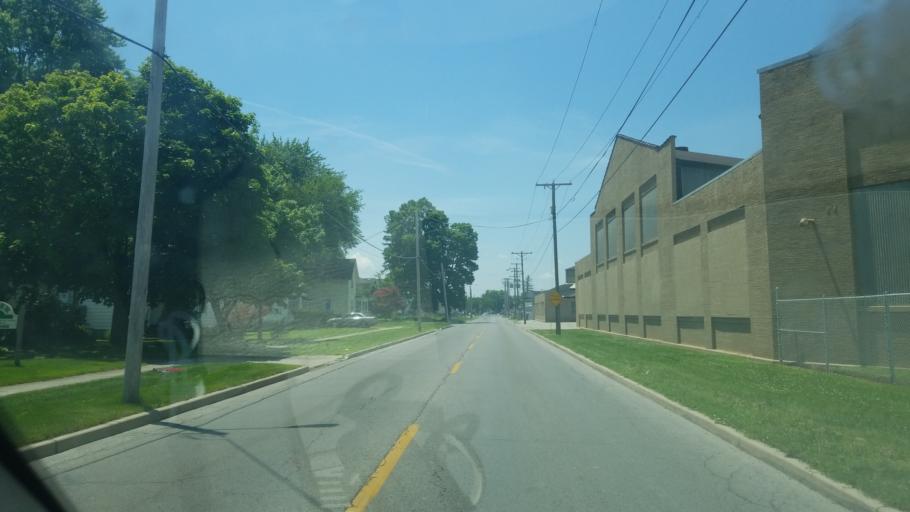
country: US
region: Ohio
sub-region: Hancock County
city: Findlay
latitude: 41.0512
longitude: -83.6434
